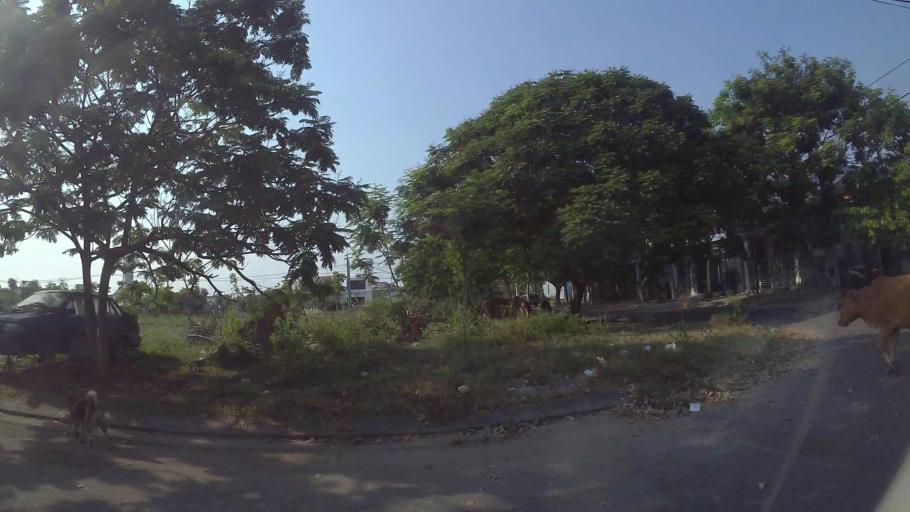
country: VN
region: Da Nang
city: Ngu Hanh Son
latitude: 15.9551
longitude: 108.2566
